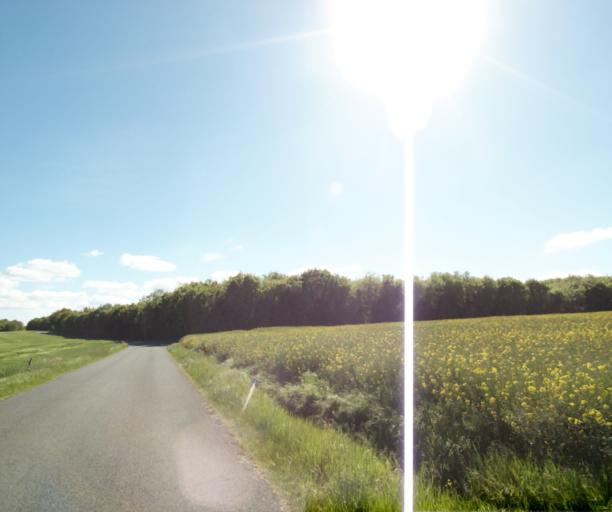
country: FR
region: Poitou-Charentes
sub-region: Departement de la Charente-Maritime
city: Bussac-sur-Charente
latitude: 45.8089
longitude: -0.6627
